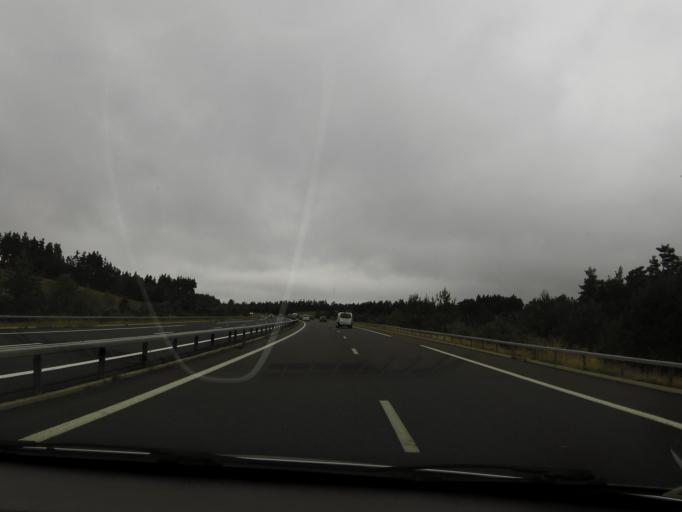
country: FR
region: Languedoc-Roussillon
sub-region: Departement de la Lozere
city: Aumont-Aubrac
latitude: 44.6810
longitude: 3.2610
